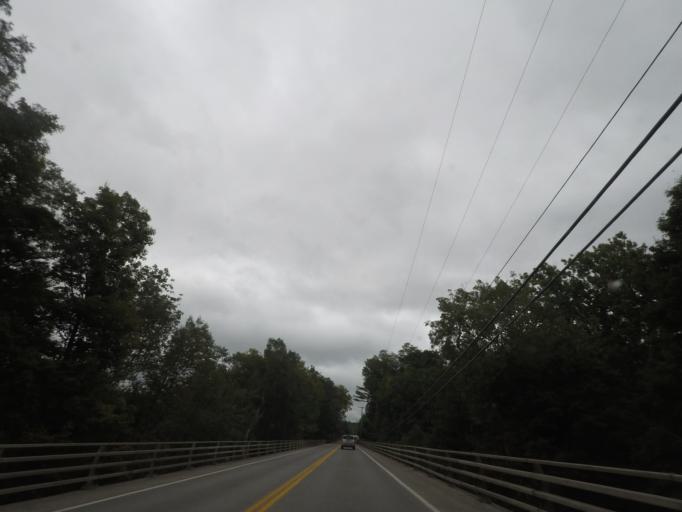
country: US
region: New York
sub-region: Rensselaer County
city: Hoosick Falls
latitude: 42.9512
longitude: -73.3831
